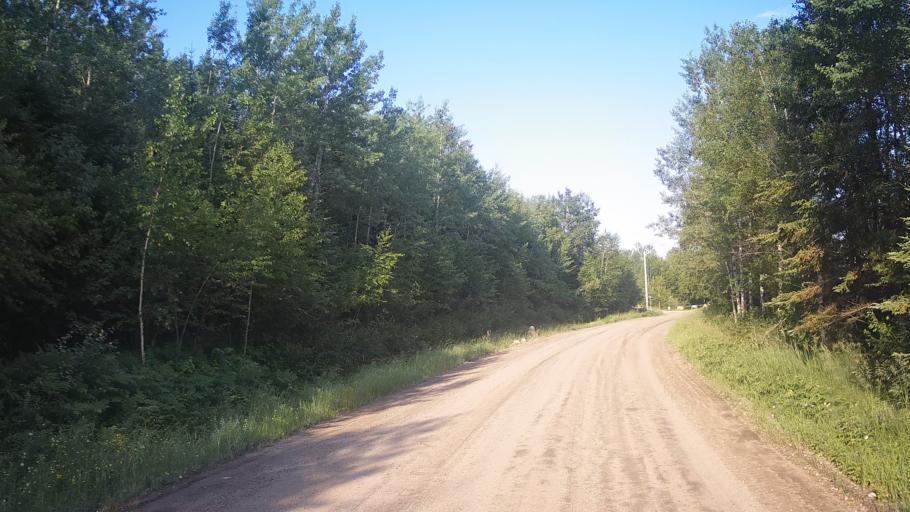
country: CA
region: Ontario
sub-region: Rainy River District
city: Atikokan
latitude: 49.3981
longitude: -91.6663
